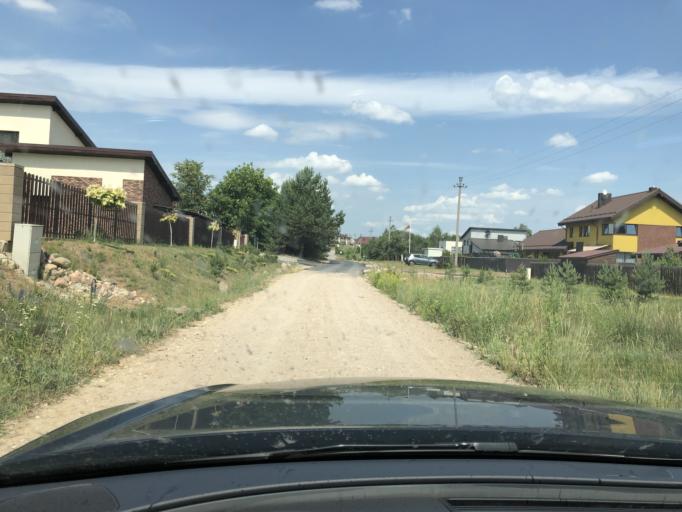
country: LT
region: Vilnius County
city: Pasilaiciai
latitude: 54.7488
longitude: 25.1907
